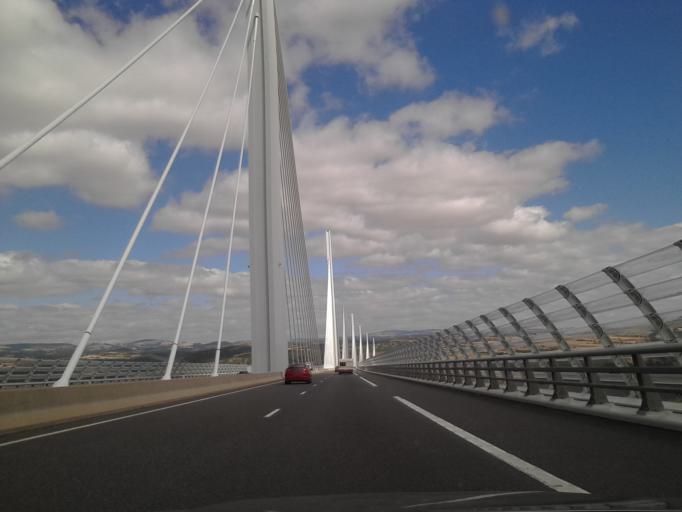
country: FR
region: Midi-Pyrenees
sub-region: Departement de l'Aveyron
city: Saint-Georges-de-Luzencon
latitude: 44.0700
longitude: 3.0245
